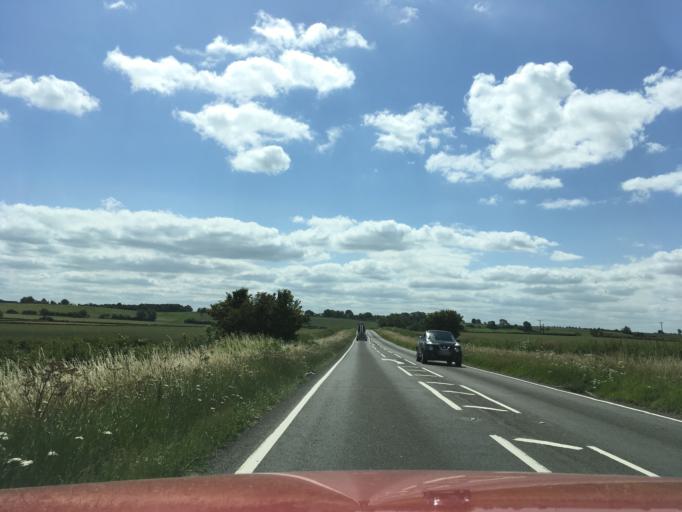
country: GB
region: England
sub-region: Buckinghamshire
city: Winslow
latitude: 51.9054
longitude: -0.8359
